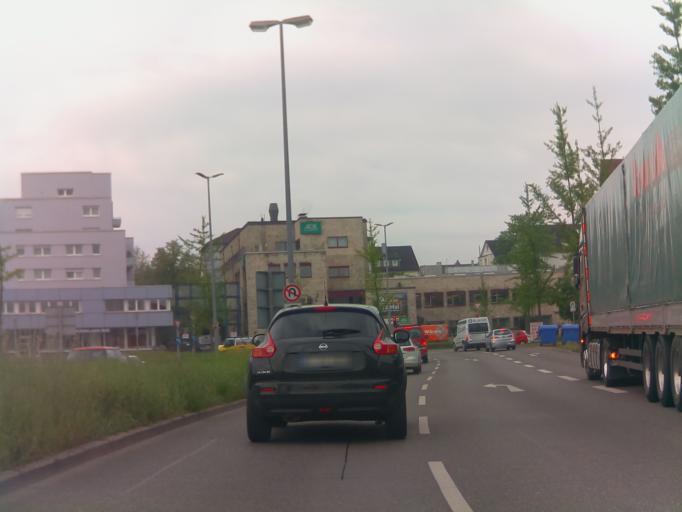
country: DE
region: Baden-Wuerttemberg
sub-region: Tuebingen Region
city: Reutlingen
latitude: 48.4921
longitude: 9.2056
